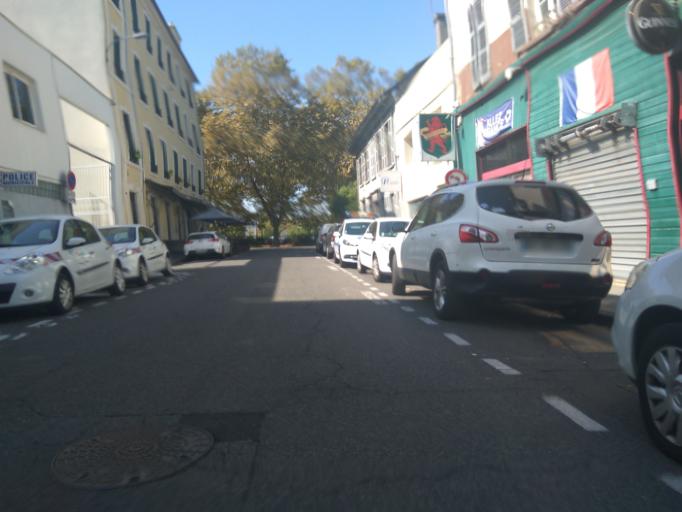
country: FR
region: Aquitaine
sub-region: Departement des Pyrenees-Atlantiques
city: Pau
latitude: 43.2999
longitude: -0.3743
